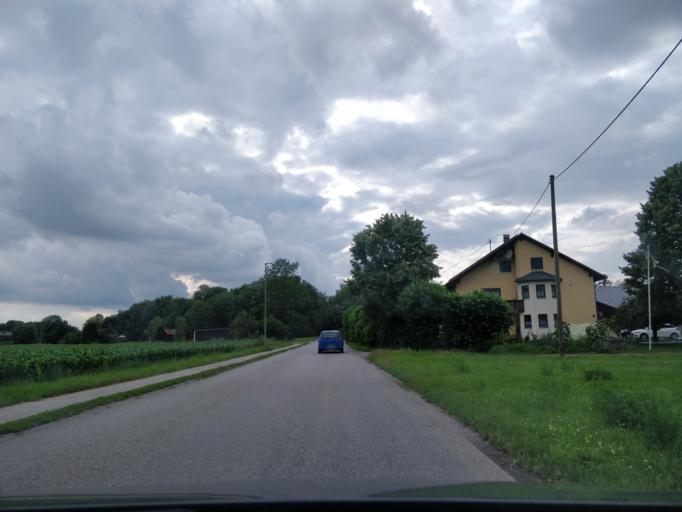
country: DE
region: Bavaria
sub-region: Swabia
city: Schmiechen
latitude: 48.2328
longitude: 10.9397
